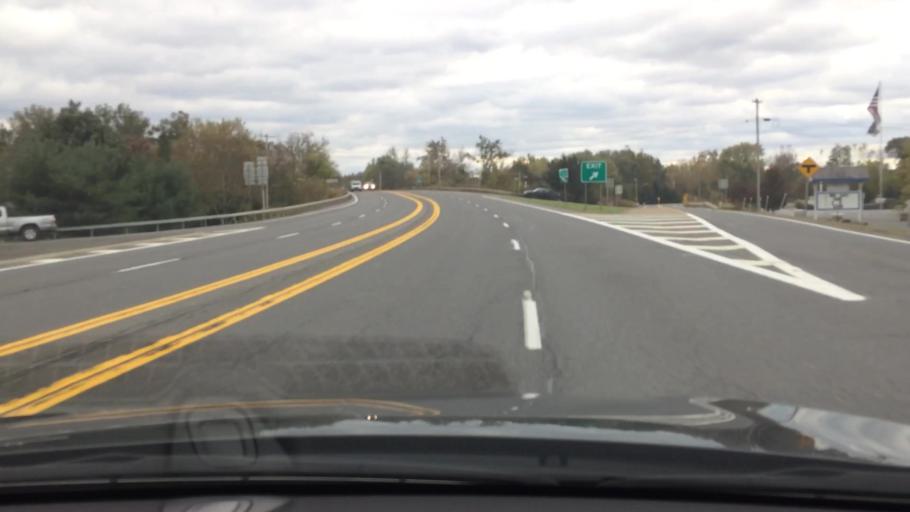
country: US
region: New York
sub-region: Columbia County
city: Kinderhook
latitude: 42.4095
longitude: -73.6913
